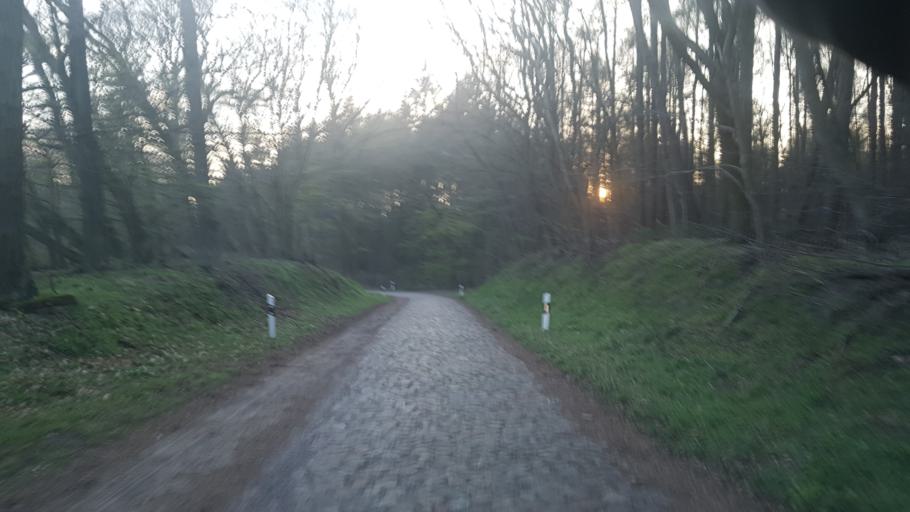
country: DE
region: Brandenburg
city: Gramzow
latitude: 53.1977
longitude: 13.9370
